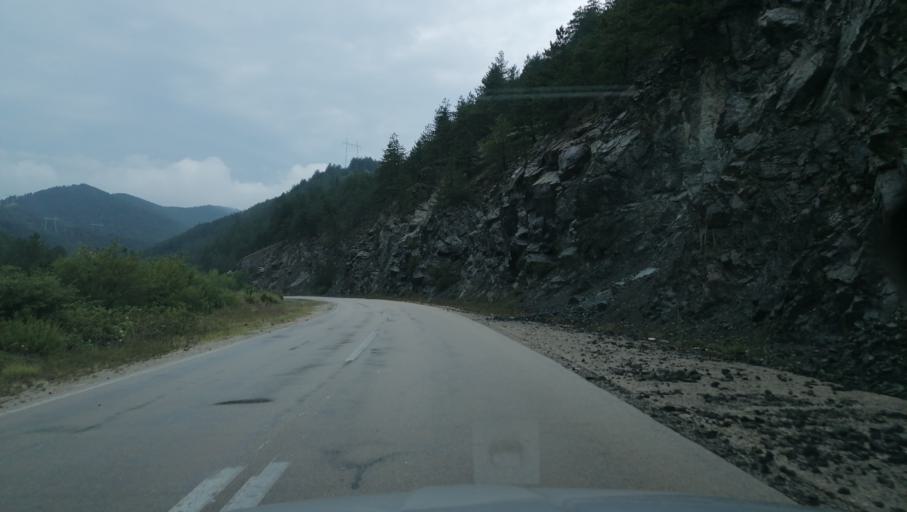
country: RS
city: Durici
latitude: 43.8309
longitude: 19.5320
